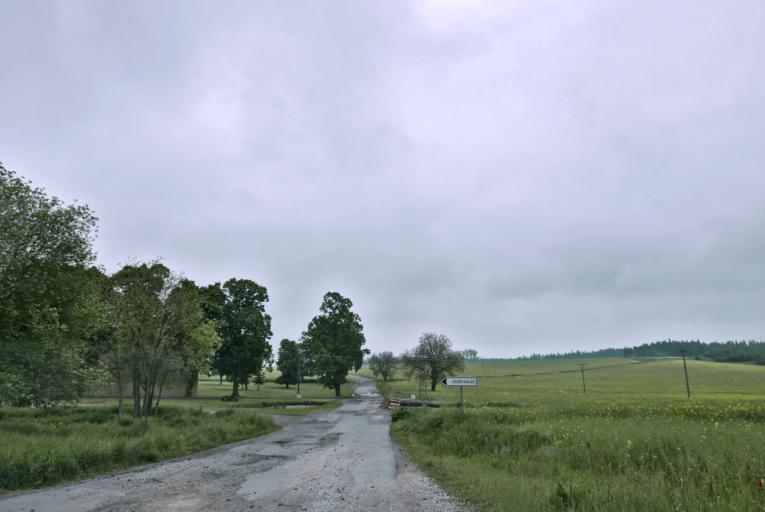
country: CZ
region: Plzensky
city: Zihle
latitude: 50.0230
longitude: 13.3272
